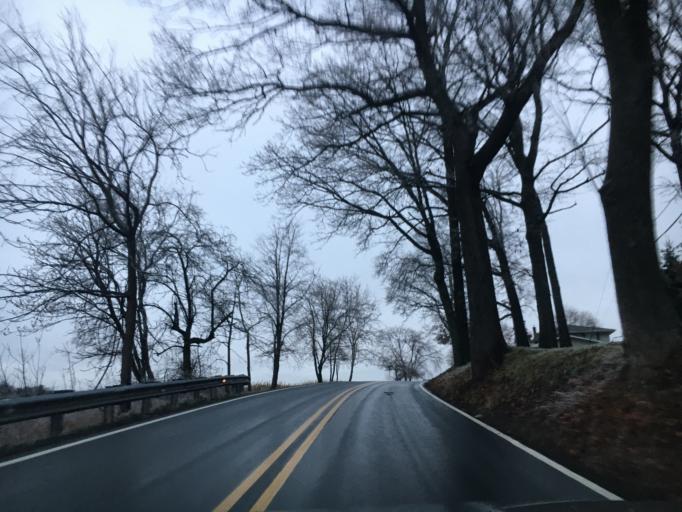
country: US
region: Pennsylvania
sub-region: Lehigh County
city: Schnecksville
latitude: 40.6438
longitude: -75.5972
